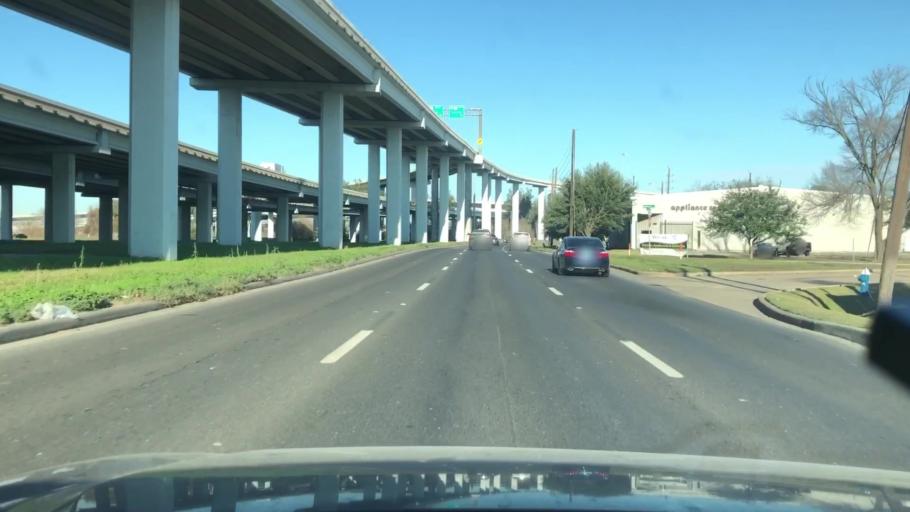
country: US
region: Texas
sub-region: Fort Bend County
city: Meadows Place
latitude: 29.6572
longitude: -95.5538
